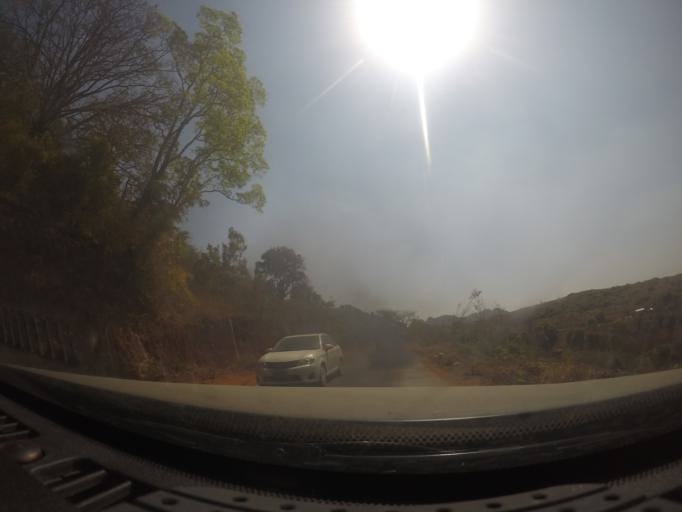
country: MM
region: Shan
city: Taunggyi
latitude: 20.8154
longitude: 97.2250
